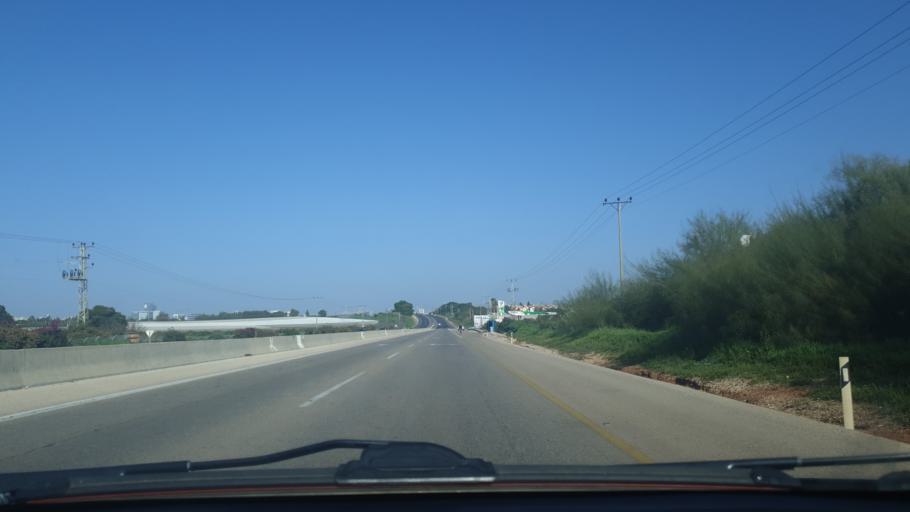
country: IL
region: Central District
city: Bet Dagan
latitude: 31.9875
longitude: 34.8309
